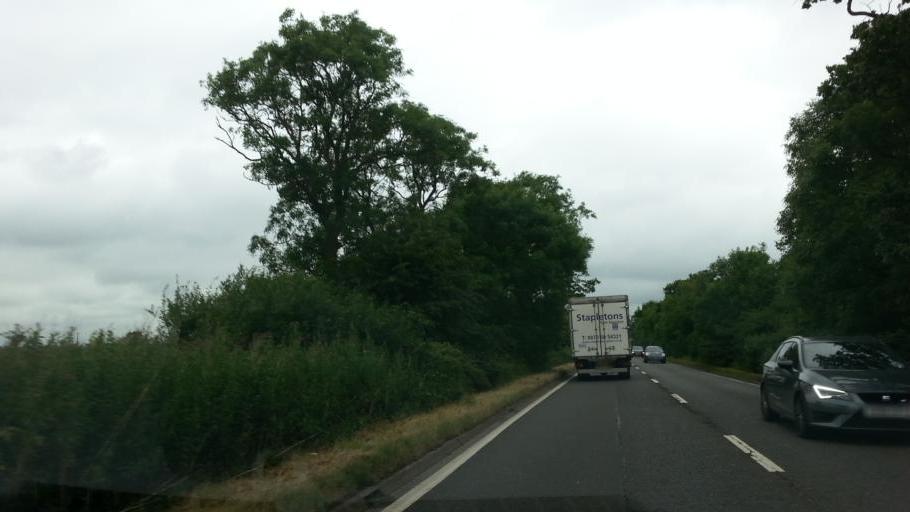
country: GB
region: England
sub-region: Northamptonshire
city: Broughton
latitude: 52.3488
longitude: -0.7892
